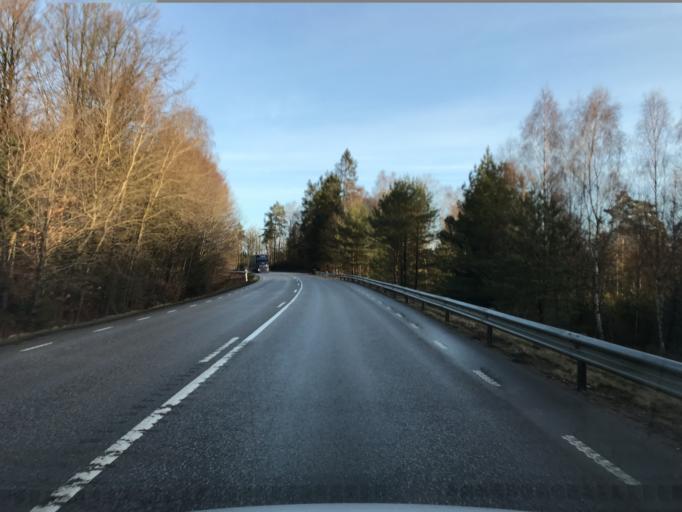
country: SE
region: Skane
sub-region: Hassleholms Kommun
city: Bjarnum
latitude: 56.2652
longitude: 13.7202
